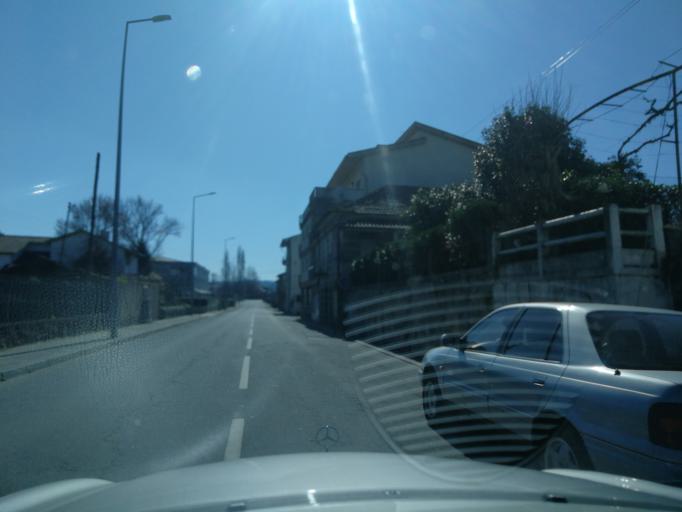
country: PT
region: Braga
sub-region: Vila Nova de Famalicao
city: Vila Nova de Famalicao
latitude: 41.3985
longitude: -8.5205
